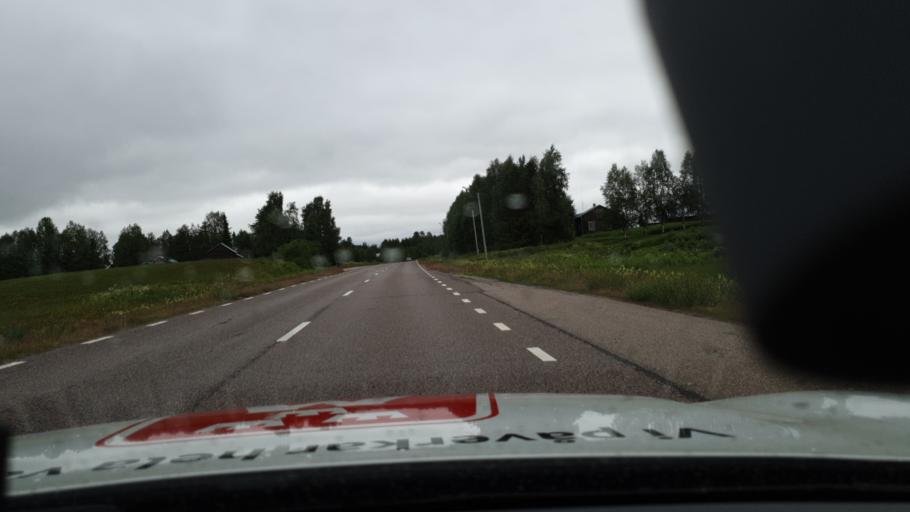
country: FI
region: Lapland
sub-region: Torniolaakso
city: Pello
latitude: 66.9641
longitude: 23.8207
